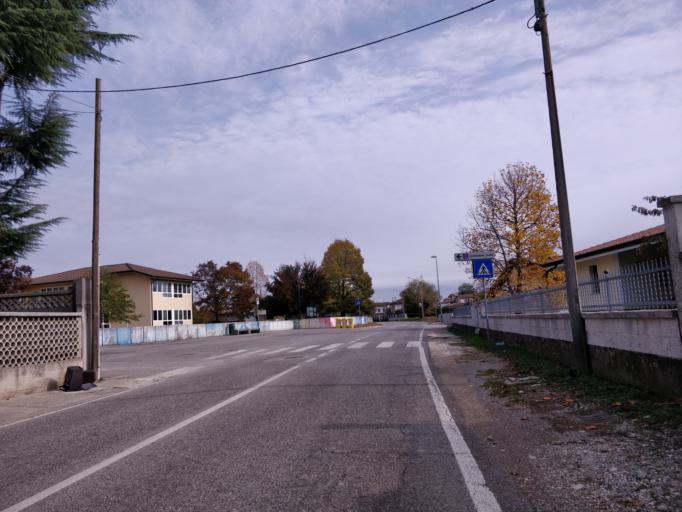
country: IT
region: Friuli Venezia Giulia
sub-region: Provincia di Udine
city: Bertiolo
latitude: 45.9441
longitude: 13.0527
